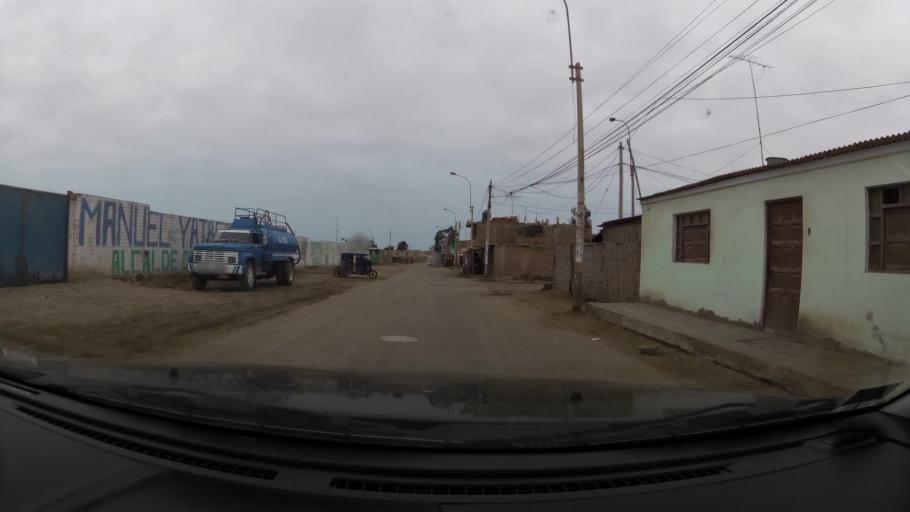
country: PE
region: Lima
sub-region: Provincia de Canete
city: Chilca
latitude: -12.5129
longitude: -76.7397
